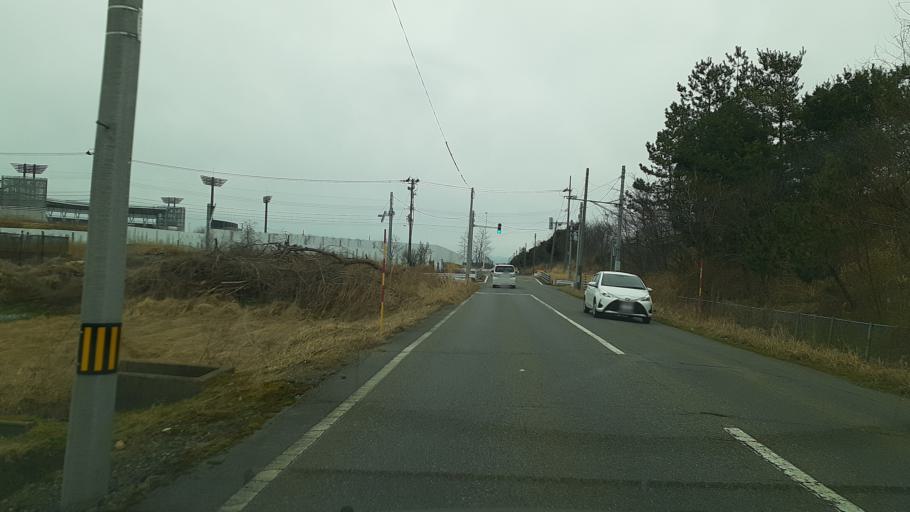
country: JP
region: Niigata
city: Niigata-shi
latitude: 37.8759
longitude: 139.0596
